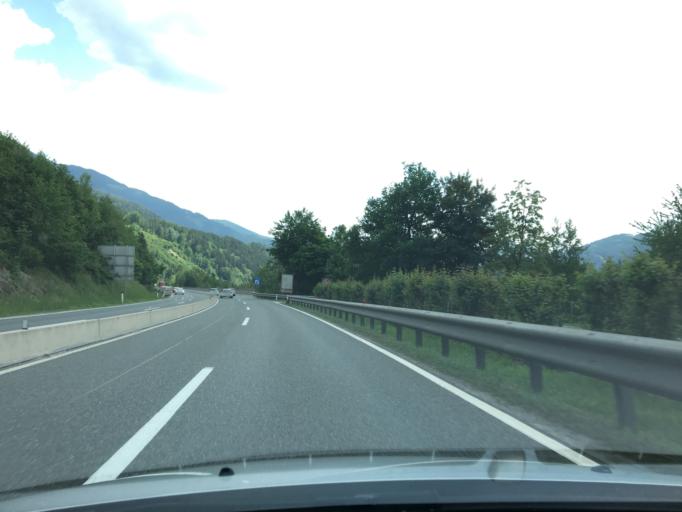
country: AT
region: Salzburg
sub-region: Politischer Bezirk Sankt Johann im Pongau
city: Bischofshofen
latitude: 47.4285
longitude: 13.2241
